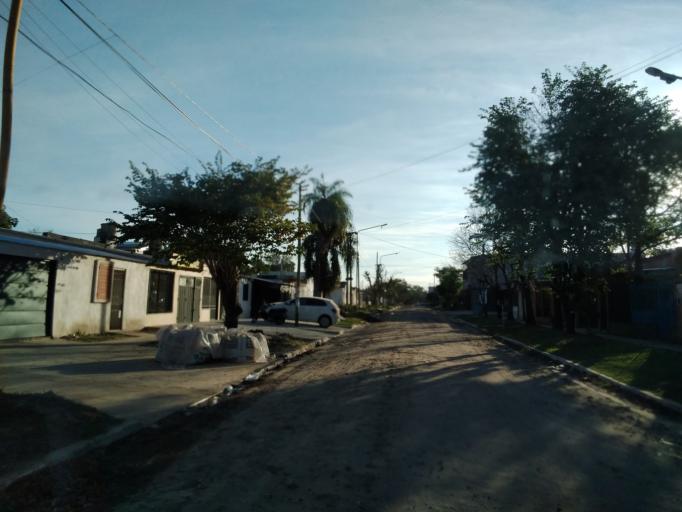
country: AR
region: Corrientes
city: Corrientes
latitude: -27.5015
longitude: -58.8323
